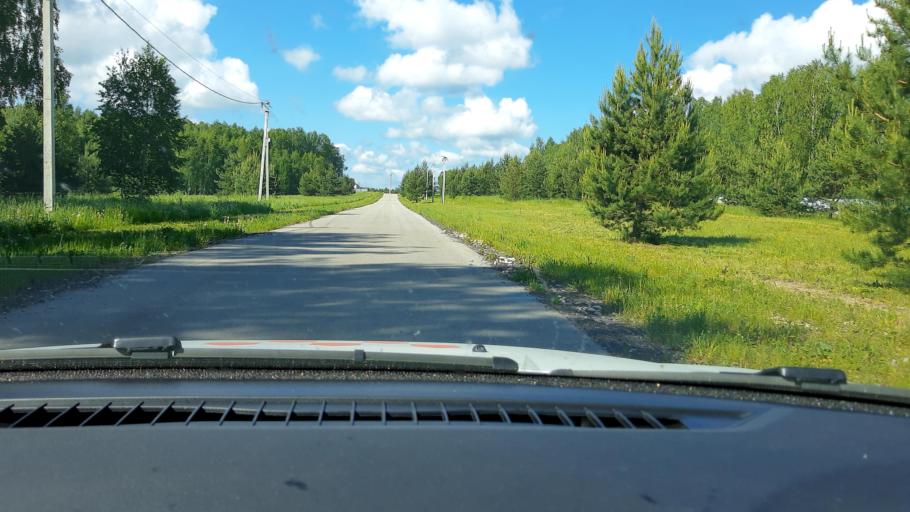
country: RU
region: Nizjnij Novgorod
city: Dal'neye Konstantinovo
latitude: 55.9296
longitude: 43.9931
